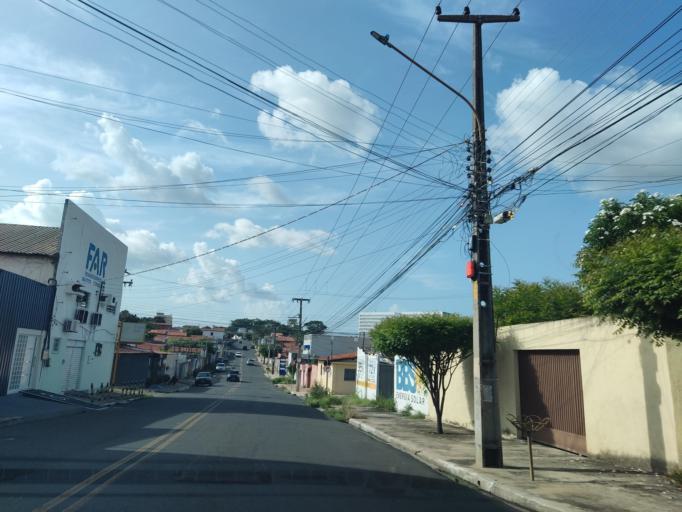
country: BR
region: Piaui
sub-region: Teresina
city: Teresina
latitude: -5.0823
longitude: -42.8017
